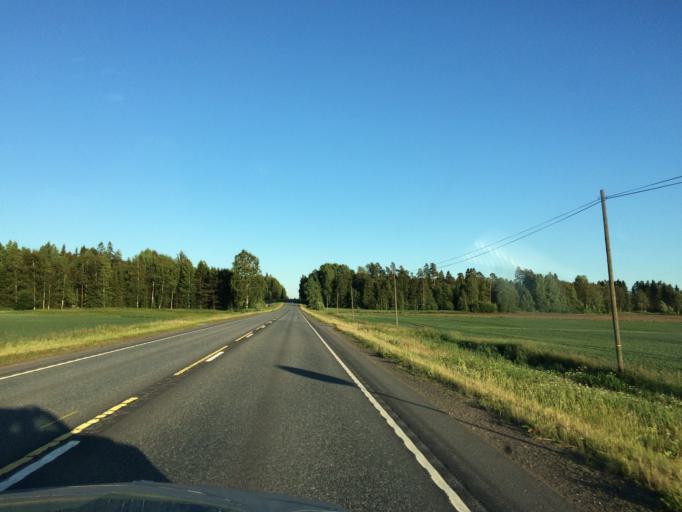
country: FI
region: Haeme
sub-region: Haemeenlinna
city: Tervakoski
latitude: 60.7954
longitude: 24.6687
